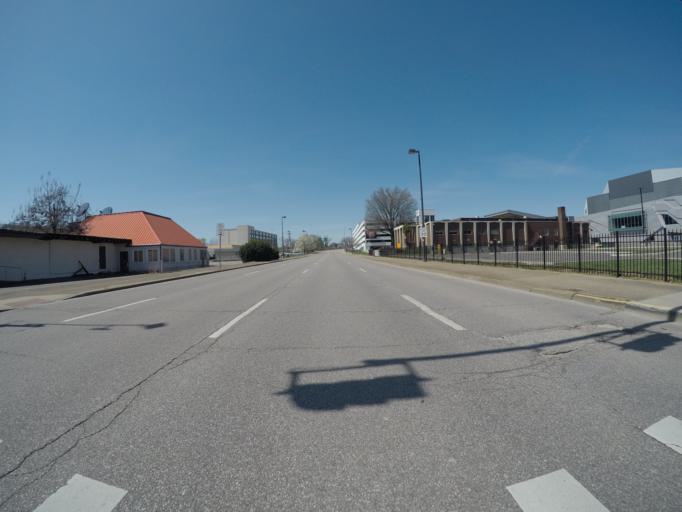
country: US
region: West Virginia
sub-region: Kanawha County
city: Charleston
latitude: 38.3544
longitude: -81.6405
